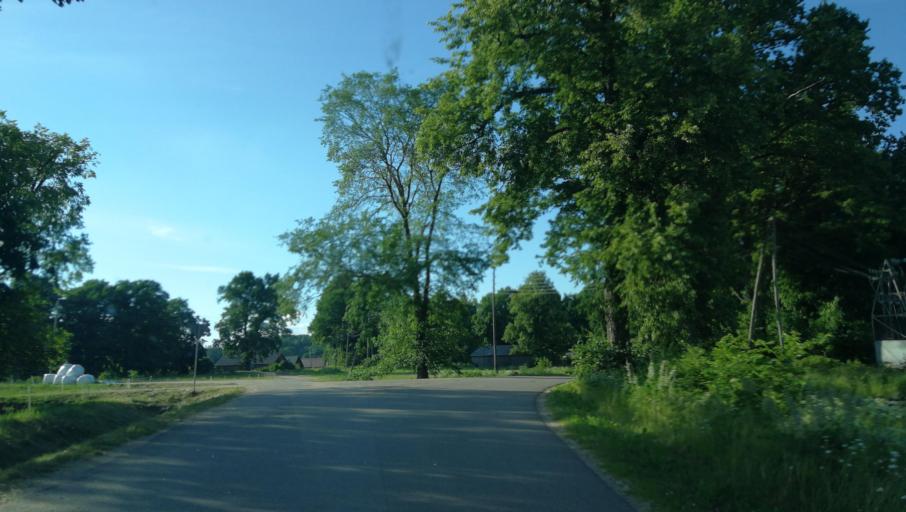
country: LV
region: Pargaujas
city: Stalbe
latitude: 57.3582
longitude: 25.0889
